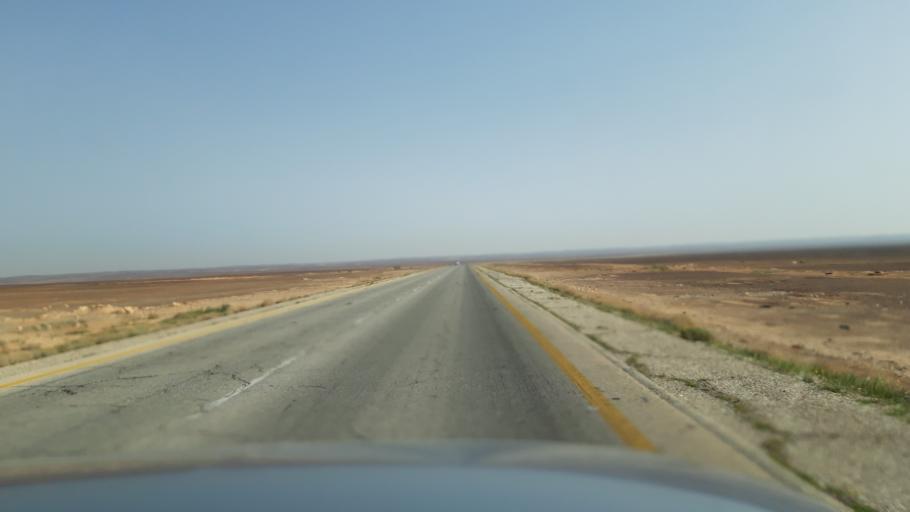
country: JO
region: Amman
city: Al Azraq ash Shamali
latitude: 31.8087
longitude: 36.5944
